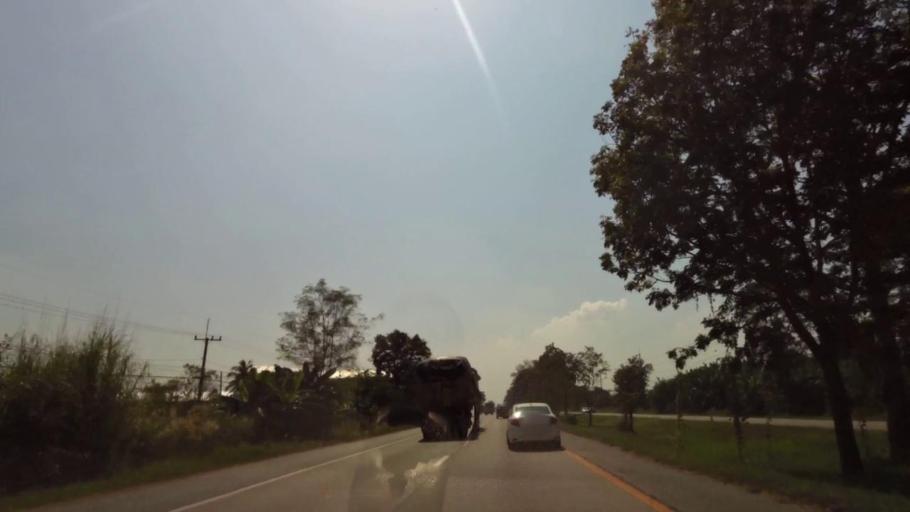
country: TH
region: Phichit
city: Wachira Barami
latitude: 16.6039
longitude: 100.1482
